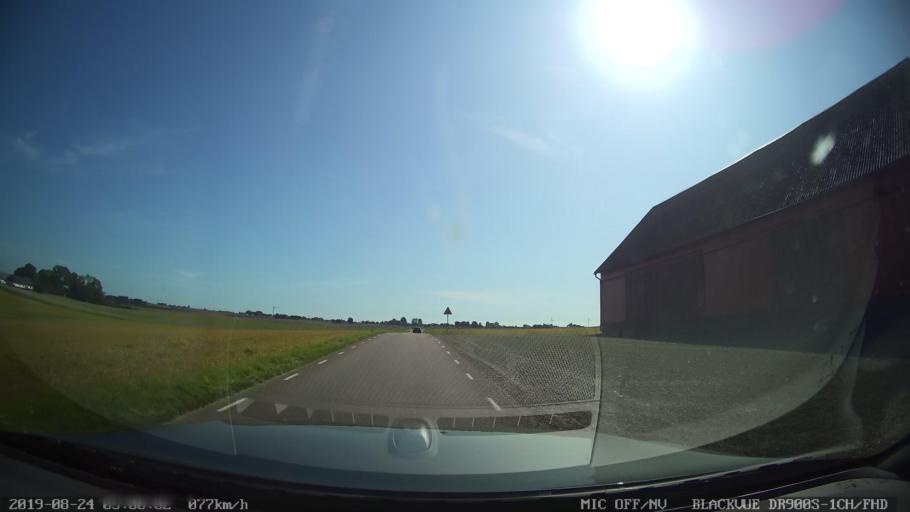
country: SE
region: Skane
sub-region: Skurups Kommun
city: Skurup
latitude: 55.4612
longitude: 13.4291
